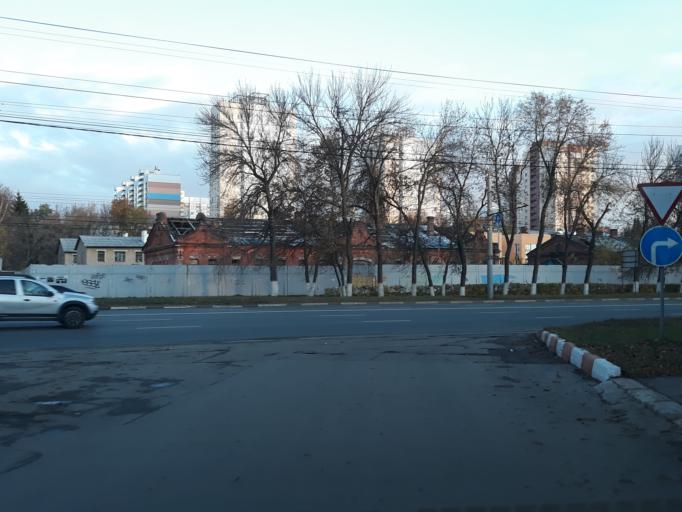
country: RU
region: Nizjnij Novgorod
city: Nizhniy Novgorod
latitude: 56.2878
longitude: 43.9808
